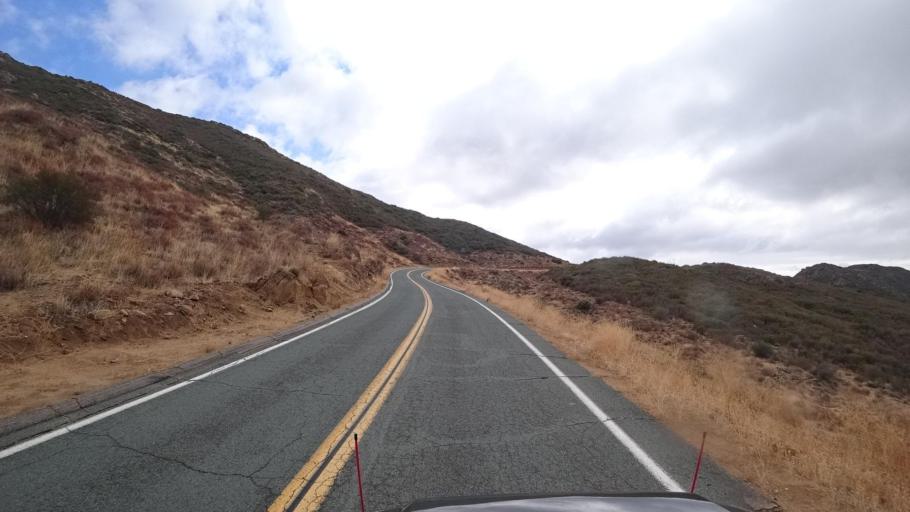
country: US
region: California
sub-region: San Diego County
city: Pine Valley
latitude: 32.7506
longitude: -116.4517
